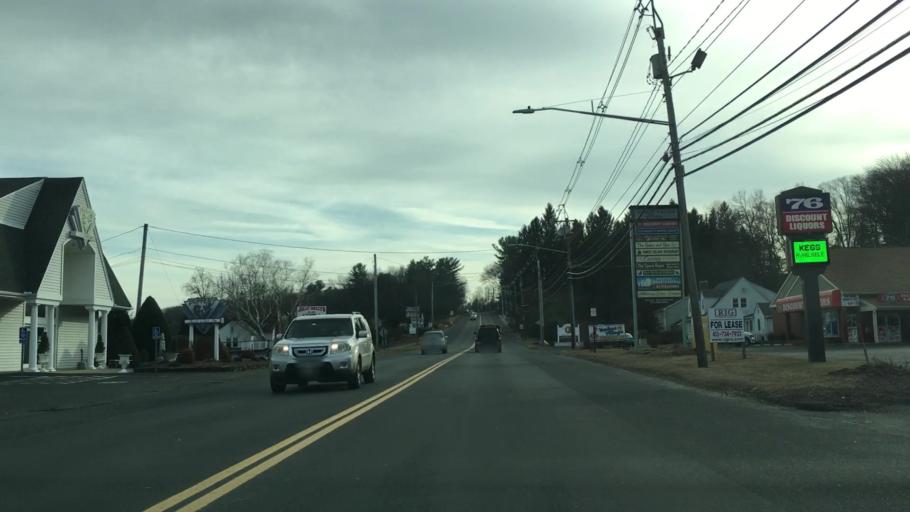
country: US
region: Massachusetts
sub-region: Hampden County
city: Westfield
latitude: 42.1092
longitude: -72.7647
